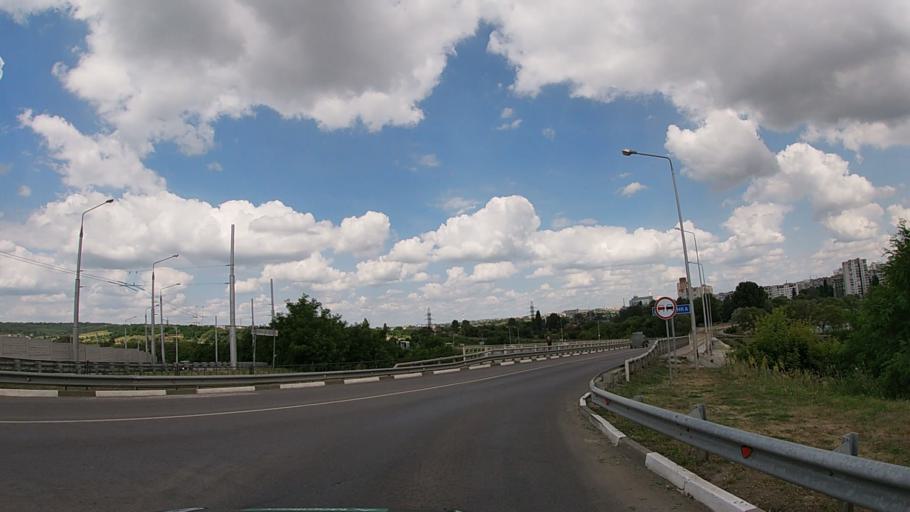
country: RU
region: Belgorod
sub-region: Belgorodskiy Rayon
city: Belgorod
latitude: 50.5899
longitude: 36.5662
